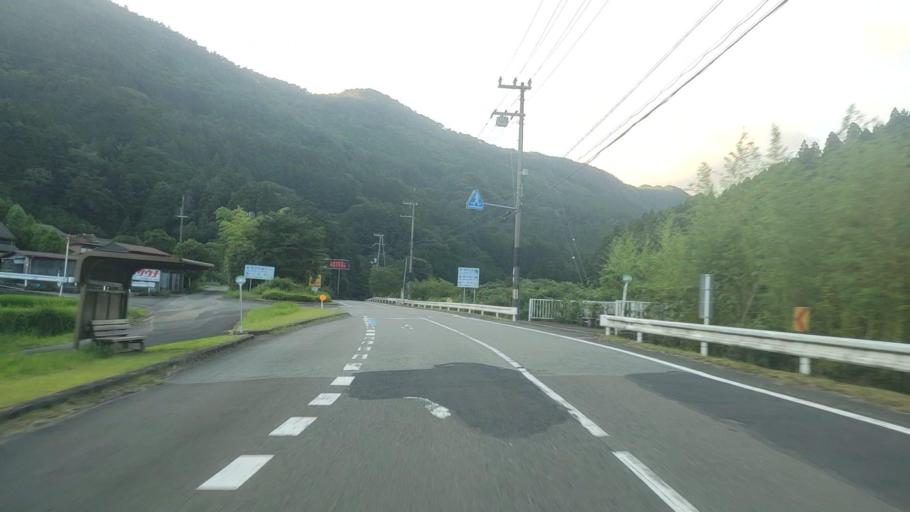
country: JP
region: Wakayama
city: Tanabe
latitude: 33.8230
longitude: 135.6312
